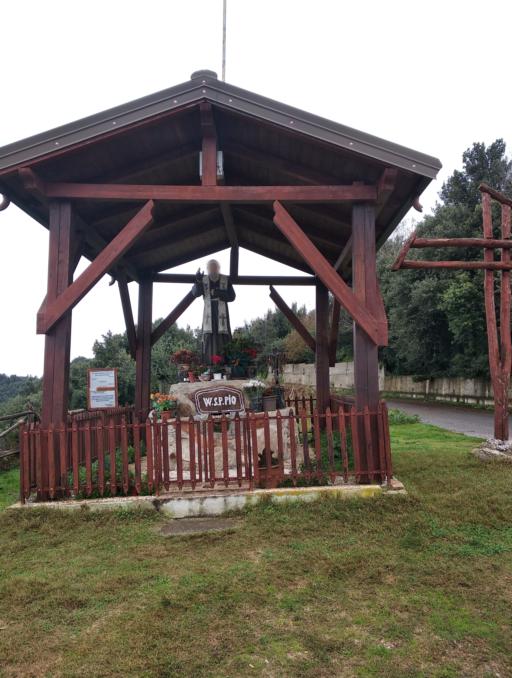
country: IT
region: Calabria
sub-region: Provincia di Reggio Calabria
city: Scilla
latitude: 38.2388
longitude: 15.7395
